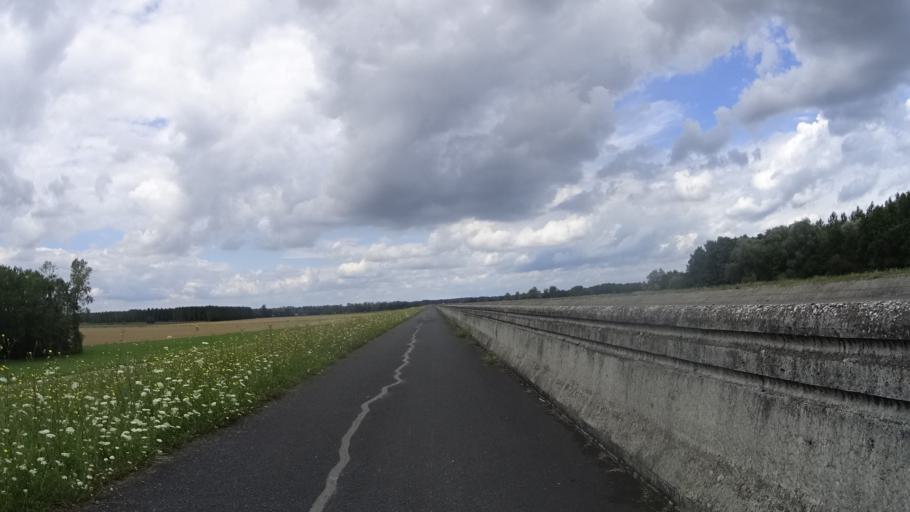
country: FR
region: Champagne-Ardenne
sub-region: Departement de la Haute-Marne
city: Villiers-en-Lieu
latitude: 48.5807
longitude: 4.8516
